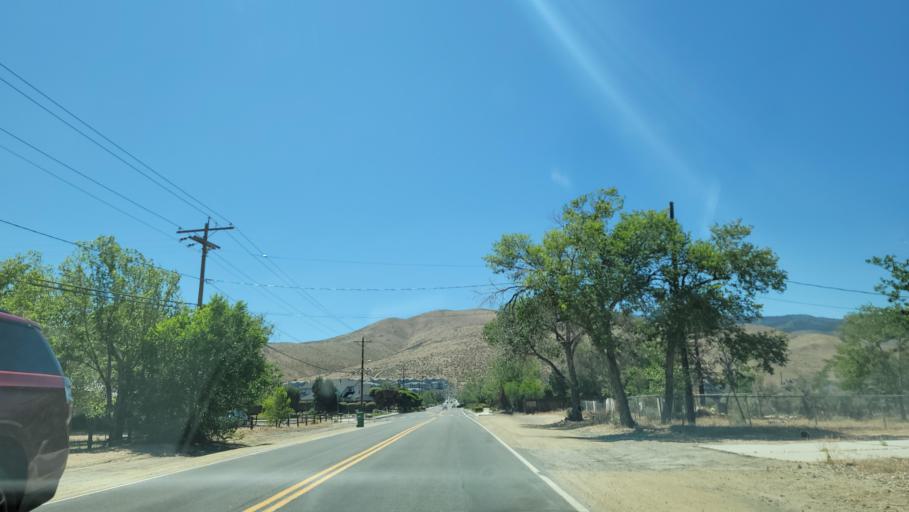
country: US
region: Nevada
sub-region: Carson City
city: Carson City
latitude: 39.1339
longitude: -119.7601
